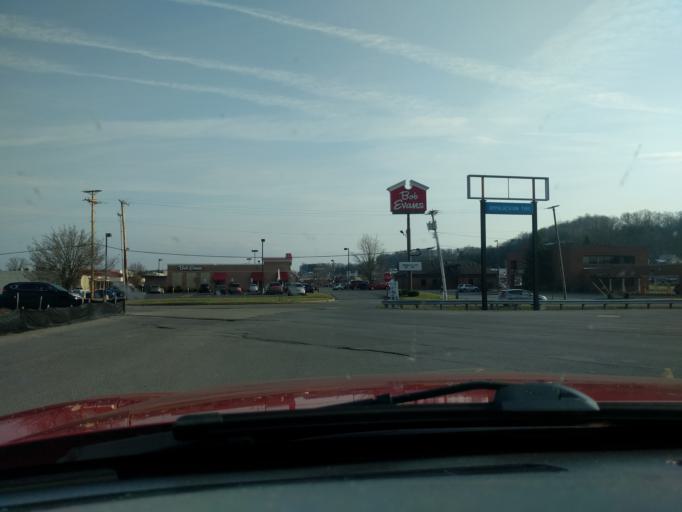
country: US
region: West Virginia
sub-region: Raleigh County
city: Prosperity
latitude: 37.8112
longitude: -81.1845
